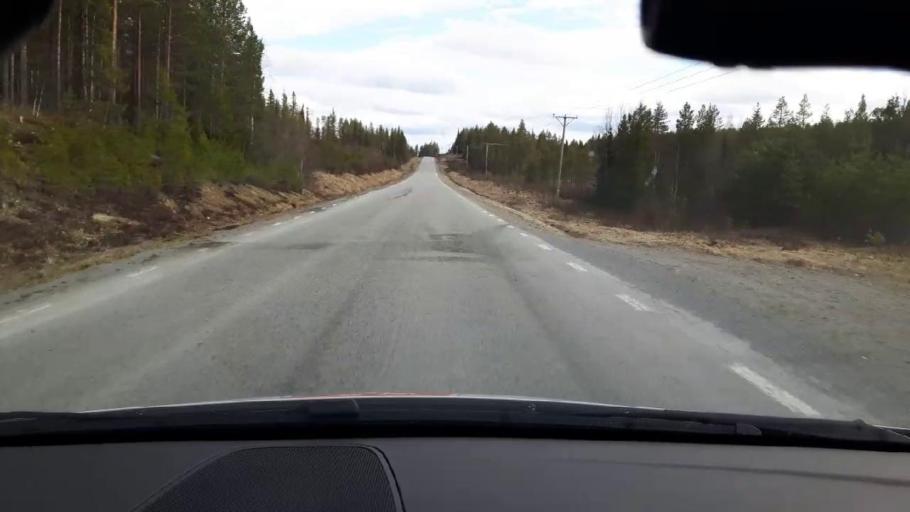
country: SE
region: Jaemtland
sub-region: Bergs Kommun
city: Hoverberg
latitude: 62.7018
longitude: 14.6210
